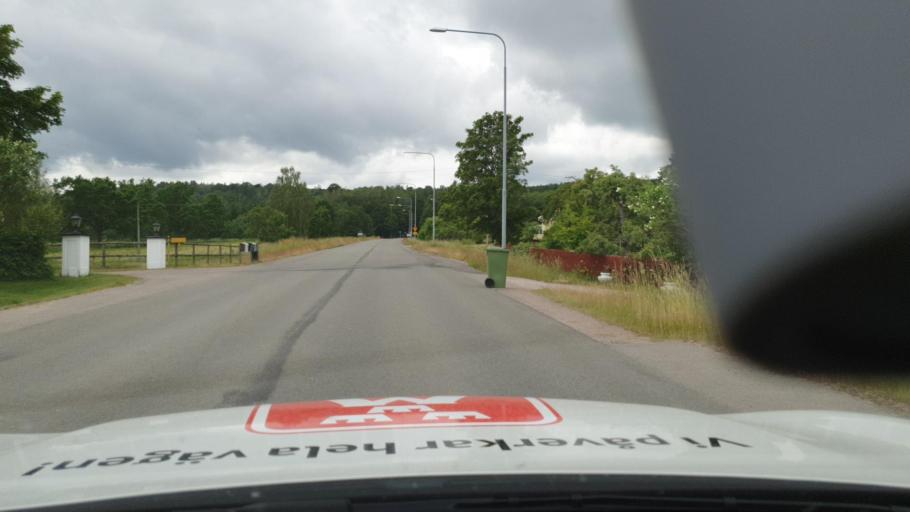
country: SE
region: Vaestra Goetaland
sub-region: Hjo Kommun
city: Hjo
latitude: 58.2898
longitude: 14.2662
